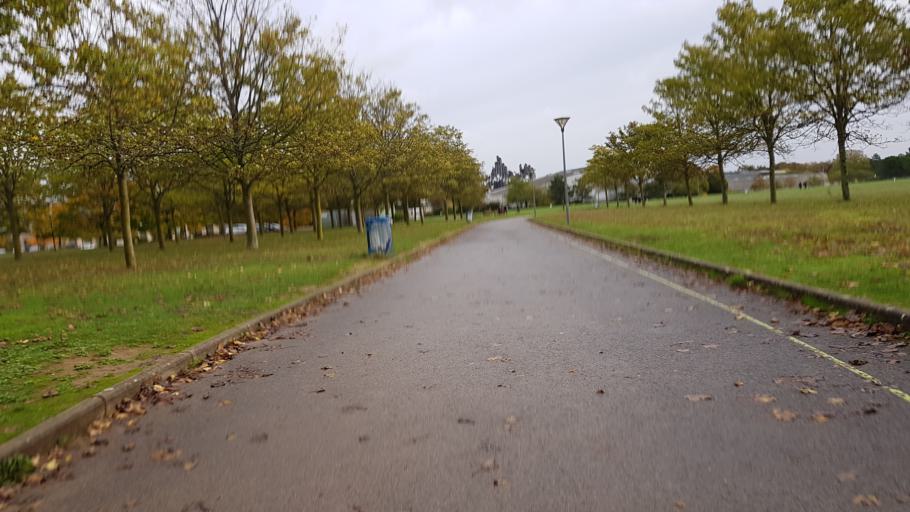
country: FR
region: Poitou-Charentes
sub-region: Departement de la Vienne
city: Jaunay-Clan
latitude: 46.6673
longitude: 0.3622
